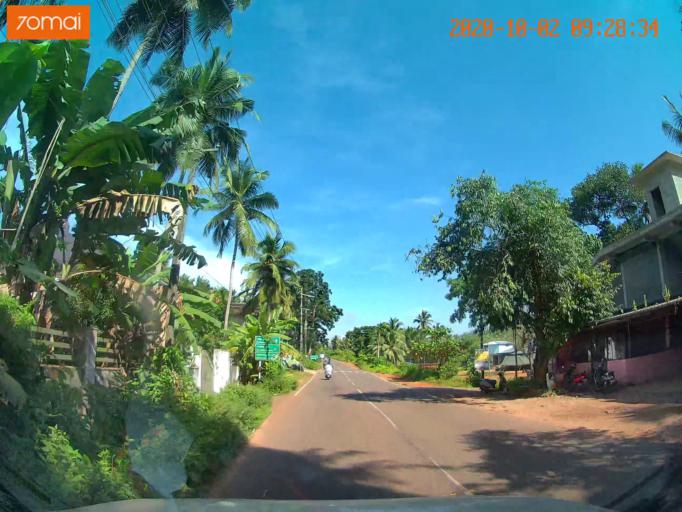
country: IN
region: Kerala
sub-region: Kozhikode
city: Naduvannur
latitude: 11.6079
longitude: 75.7628
